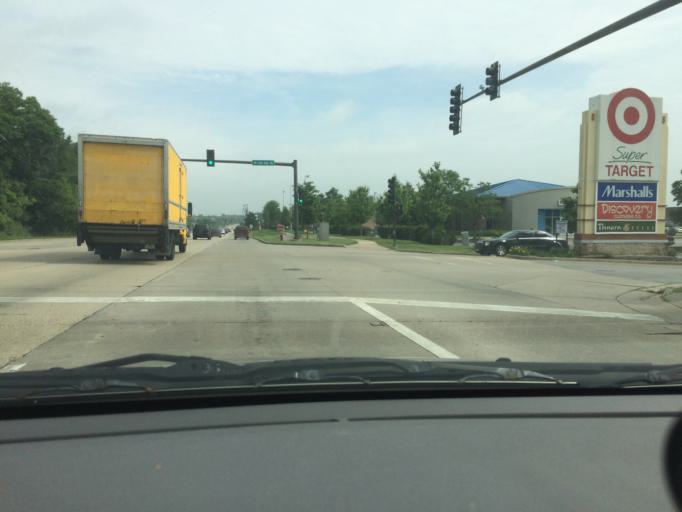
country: US
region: Illinois
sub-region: Cook County
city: Streamwood
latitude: 42.0159
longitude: -88.2030
